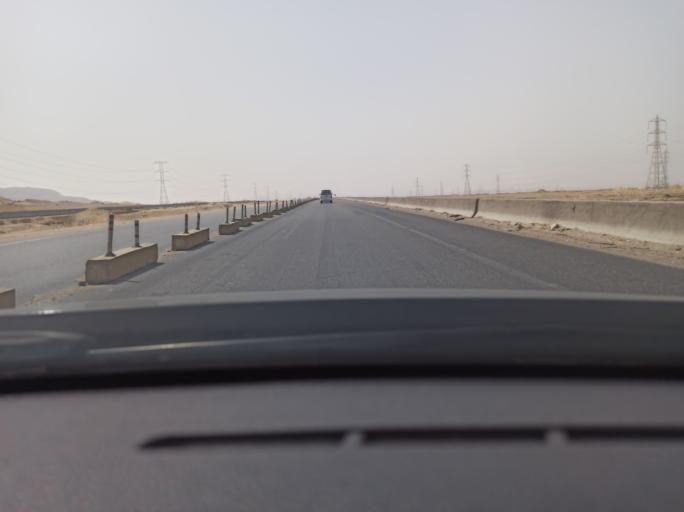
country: EG
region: Muhafazat Bani Suwayf
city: Bush
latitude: 29.1141
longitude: 31.2193
